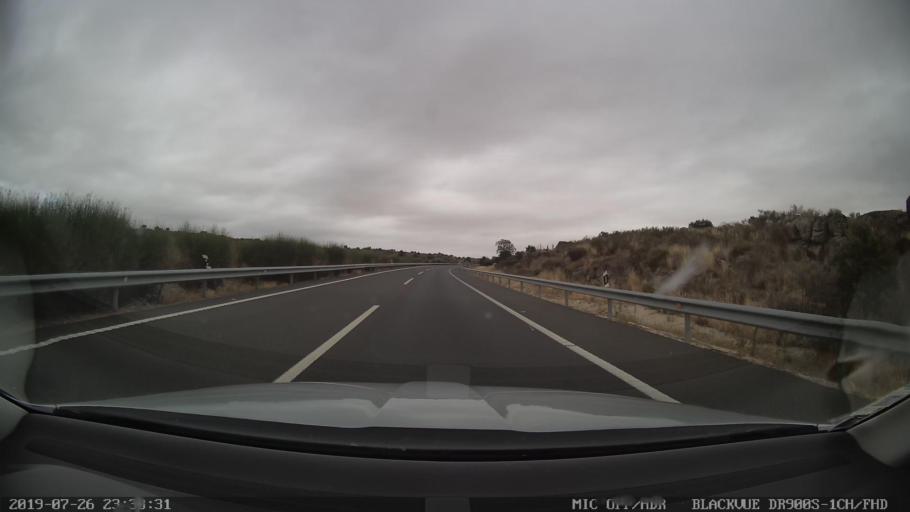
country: ES
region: Extremadura
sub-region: Provincia de Caceres
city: Trujillo
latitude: 39.4320
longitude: -5.8782
